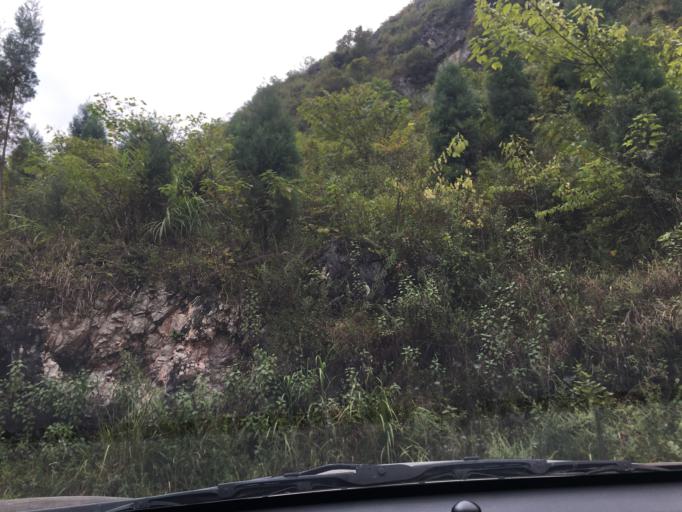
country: CN
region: Guangxi Zhuangzu Zizhiqu
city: Xinzhou
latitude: 25.3806
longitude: 105.6352
